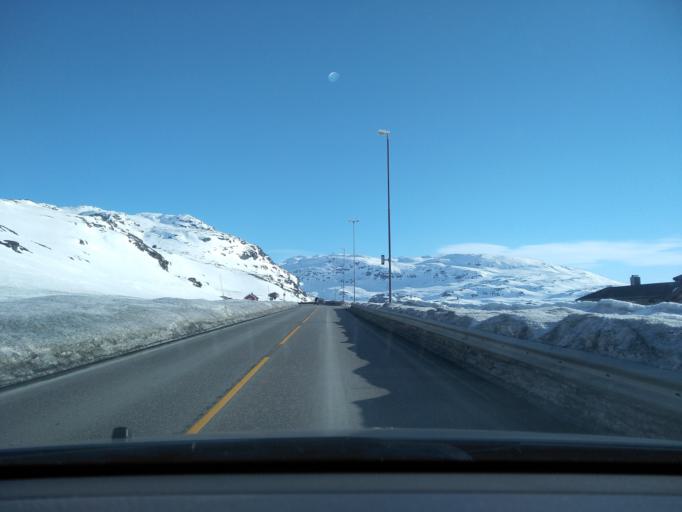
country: NO
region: Aust-Agder
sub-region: Bykle
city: Hovden
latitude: 59.8405
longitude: 6.9835
